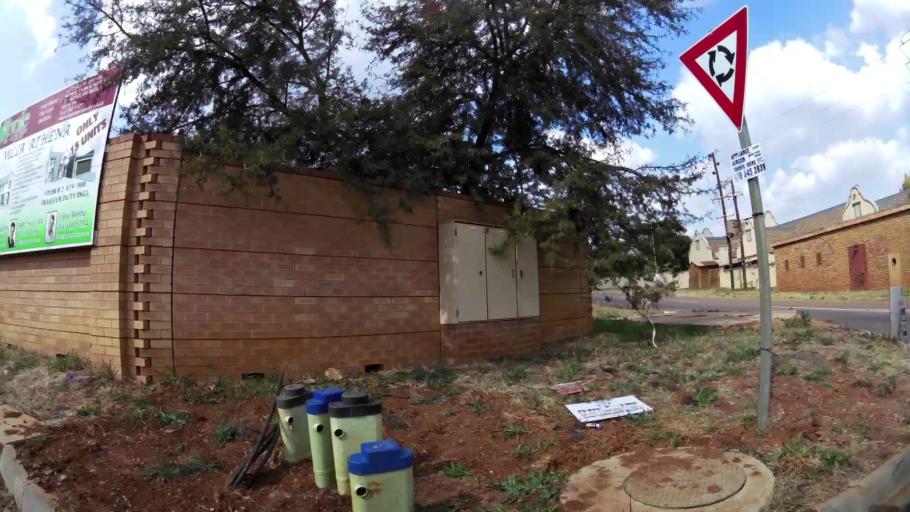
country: ZA
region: Gauteng
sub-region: City of Tshwane Metropolitan Municipality
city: Pretoria
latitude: -25.8013
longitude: 28.3438
